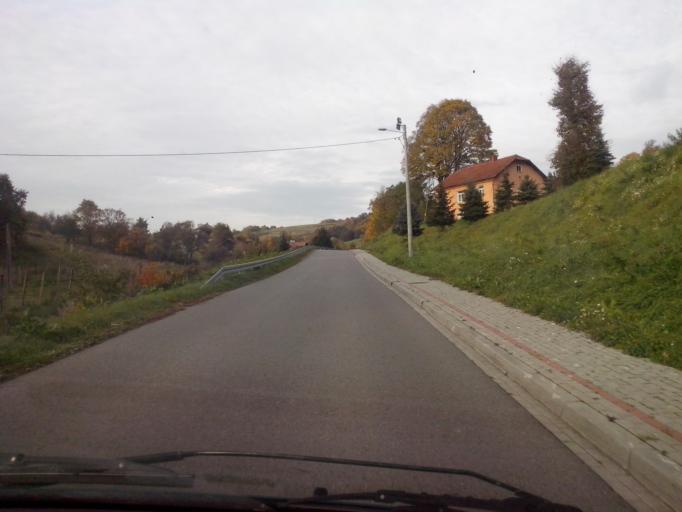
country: PL
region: Subcarpathian Voivodeship
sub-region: Powiat strzyzowski
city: Wisniowa
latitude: 49.8838
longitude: 21.6700
